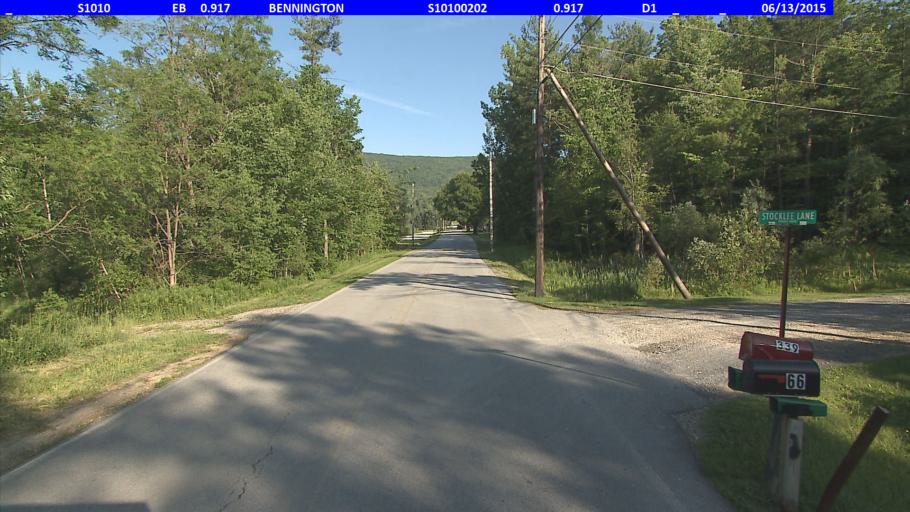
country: US
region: Vermont
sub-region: Bennington County
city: Bennington
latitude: 42.8758
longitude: -73.1586
